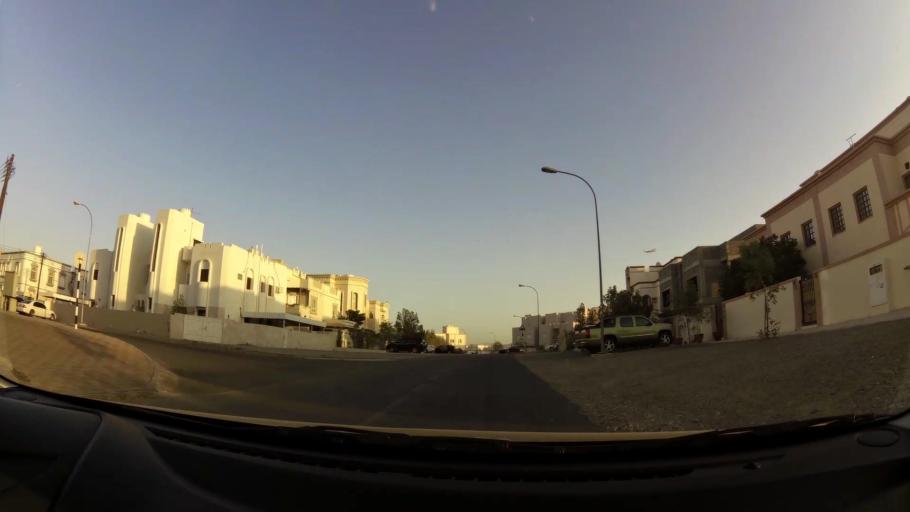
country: OM
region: Muhafazat Masqat
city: As Sib al Jadidah
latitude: 23.6138
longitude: 58.1955
